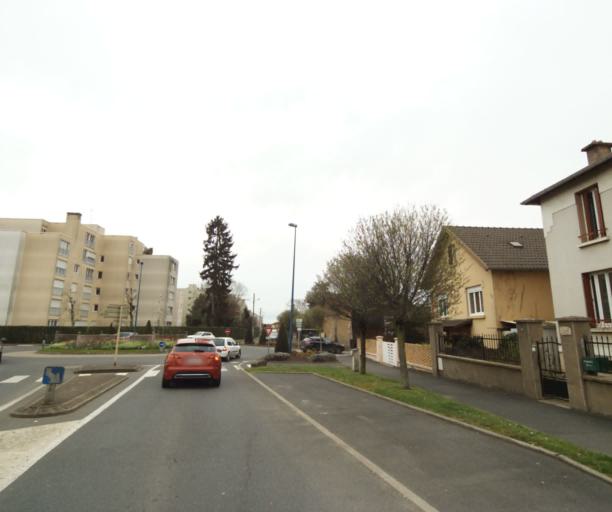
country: FR
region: Bourgogne
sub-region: Departement de Saone-et-Loire
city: Charnay-les-Macon
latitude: 46.3117
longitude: 4.8102
